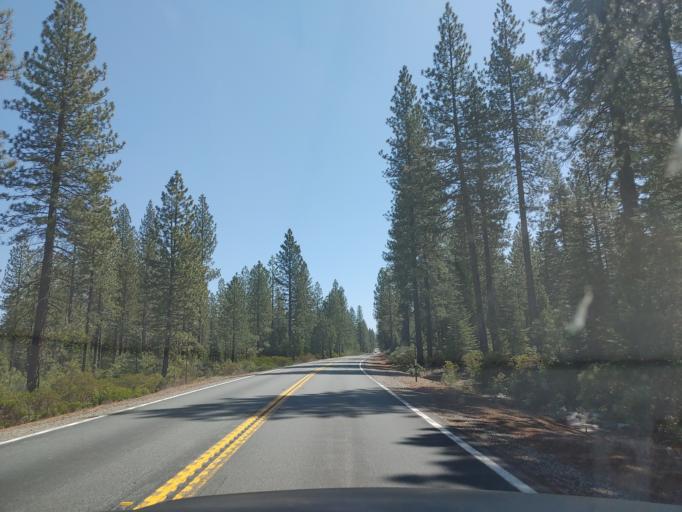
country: US
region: California
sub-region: Siskiyou County
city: McCloud
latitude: 41.2656
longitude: -121.8553
